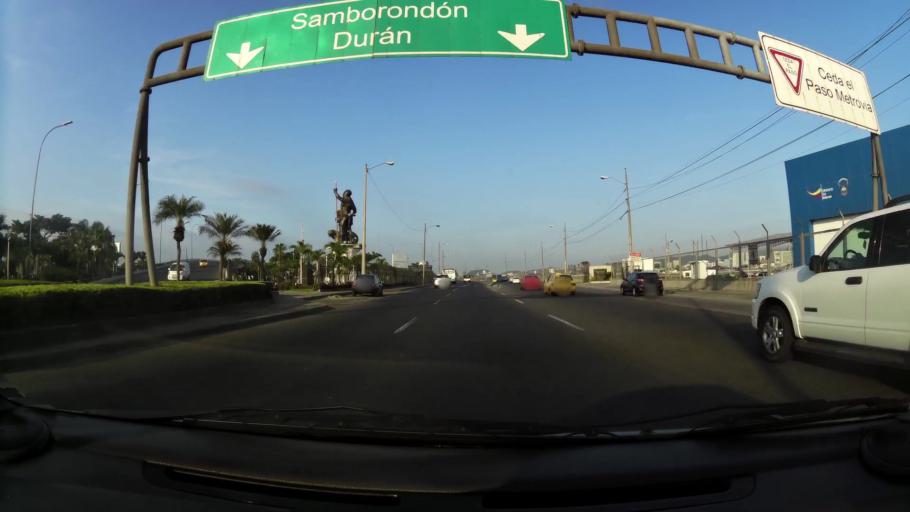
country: EC
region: Guayas
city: Eloy Alfaro
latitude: -2.1540
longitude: -79.8789
